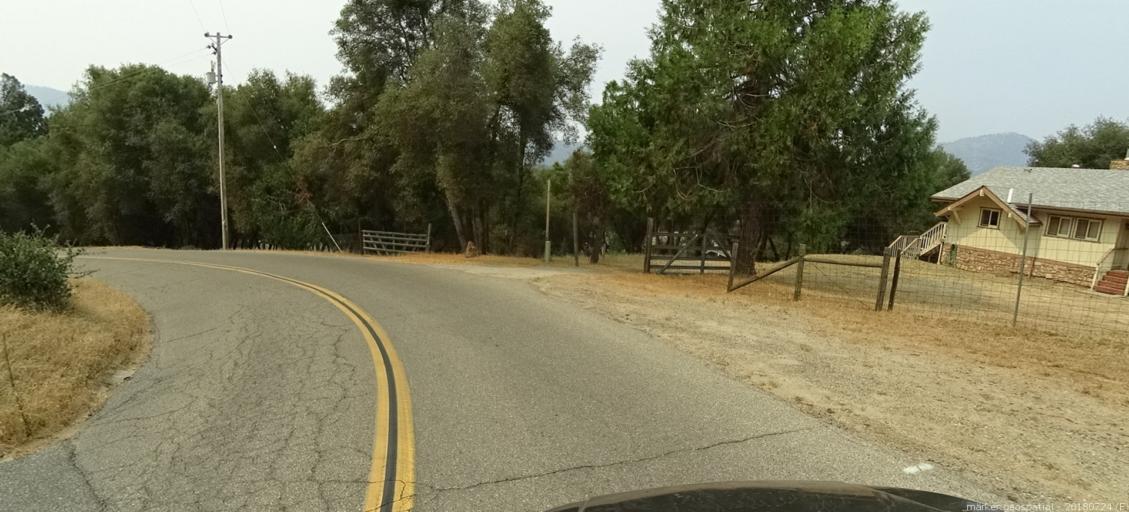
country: US
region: California
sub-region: Madera County
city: Oakhurst
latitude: 37.3282
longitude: -119.6173
